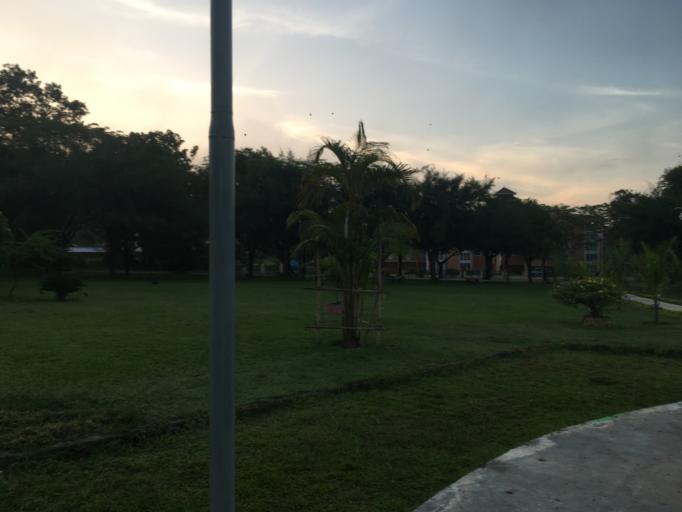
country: MM
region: Mon
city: Mawlamyine
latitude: 16.4665
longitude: 97.6278
